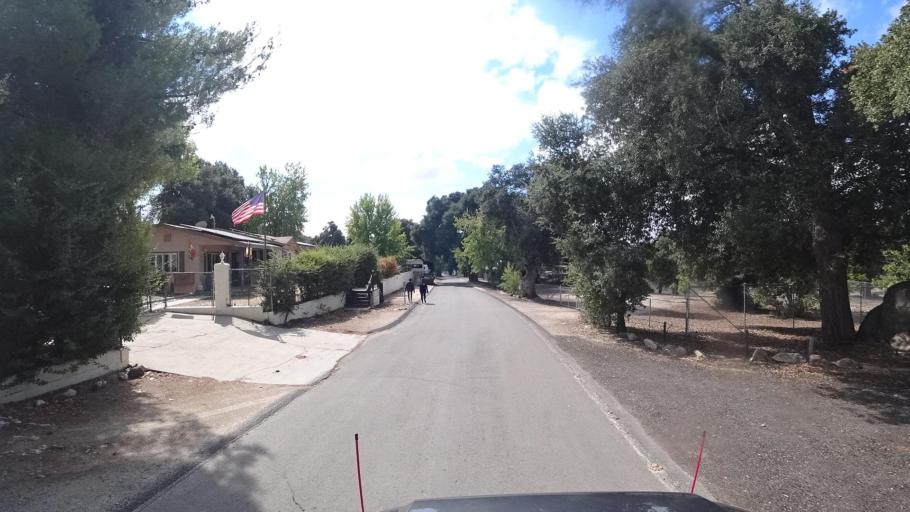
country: US
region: California
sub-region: San Diego County
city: Campo
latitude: 32.6922
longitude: -116.3341
